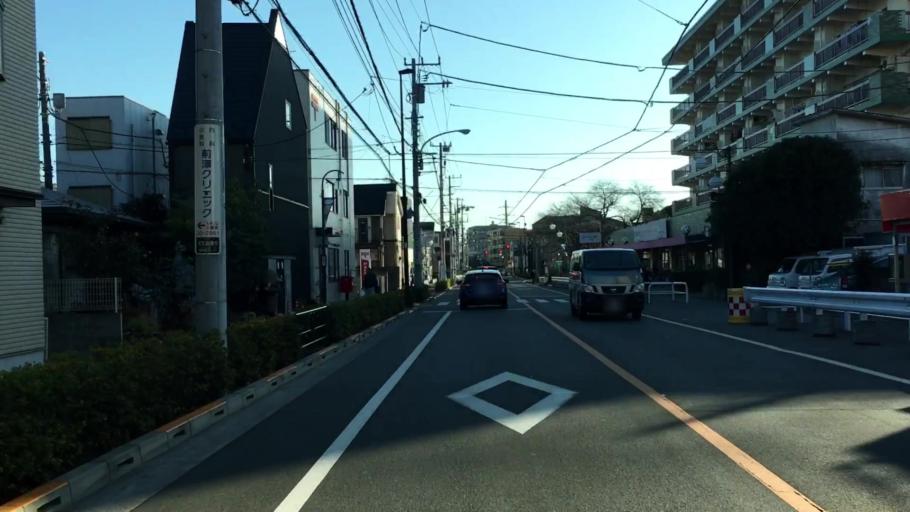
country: JP
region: Tokyo
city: Kamirenjaku
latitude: 35.6996
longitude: 139.5383
